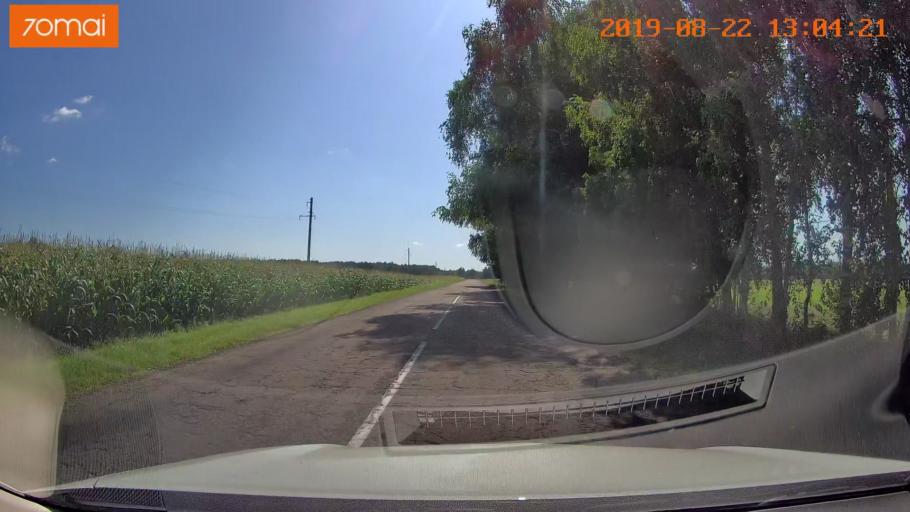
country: BY
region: Minsk
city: Prawdzinski
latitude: 53.3717
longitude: 27.8255
